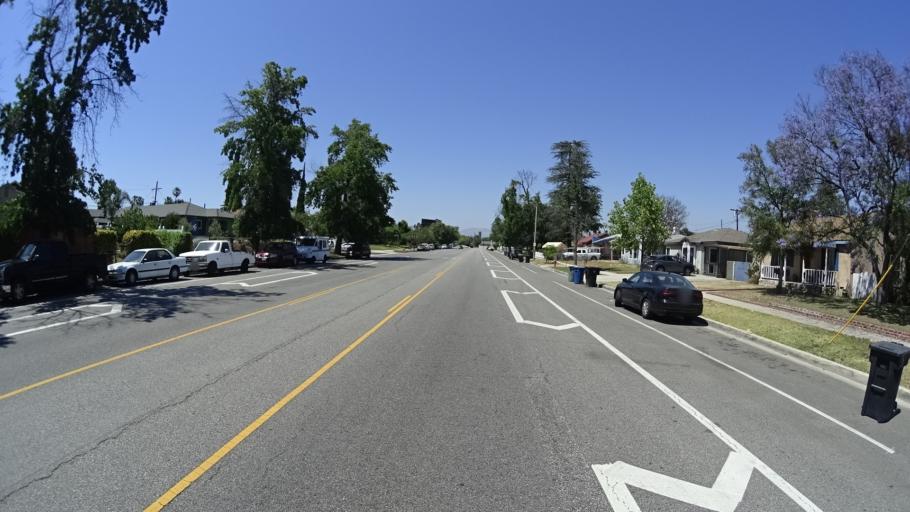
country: US
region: California
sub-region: Los Angeles County
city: North Hollywood
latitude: 34.1823
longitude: -118.3593
